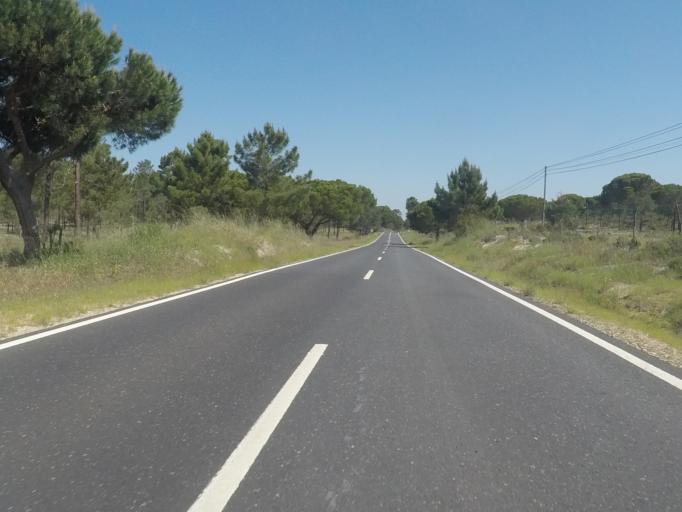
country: PT
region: Setubal
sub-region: Grandola
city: Grandola
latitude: 38.2827
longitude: -8.7259
